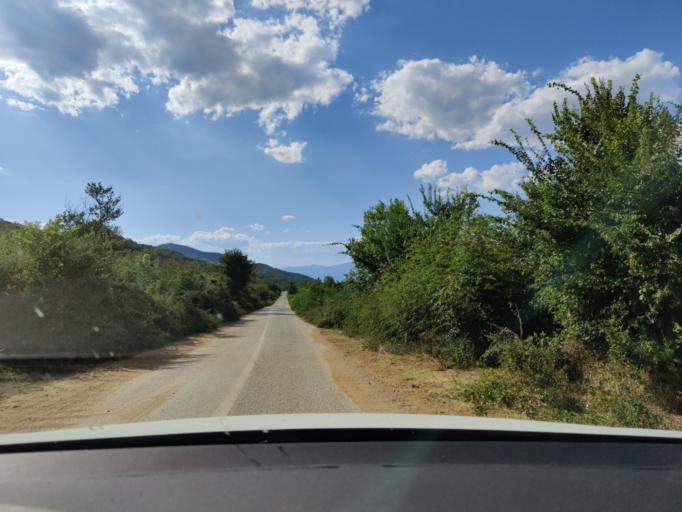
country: GR
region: Central Macedonia
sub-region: Nomos Serron
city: Chrysochorafa
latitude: 41.1542
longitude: 23.1980
